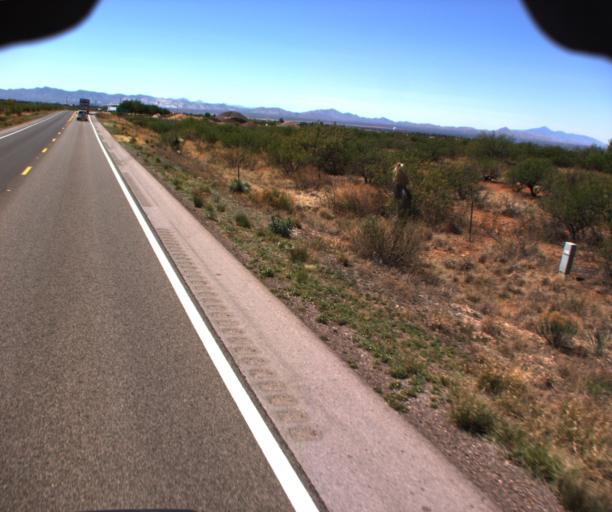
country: US
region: Arizona
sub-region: Cochise County
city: Douglas
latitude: 31.3869
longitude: -109.5143
